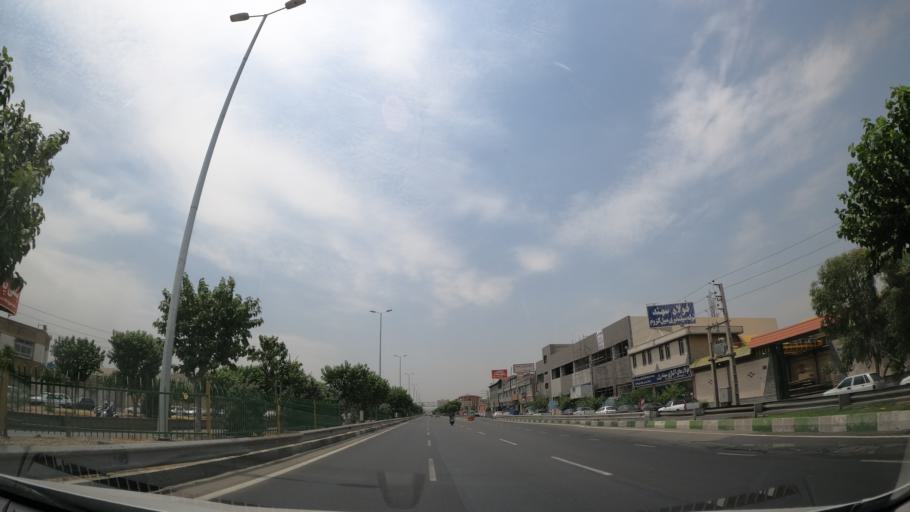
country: IR
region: Tehran
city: Tehran
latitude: 35.6751
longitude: 51.3195
